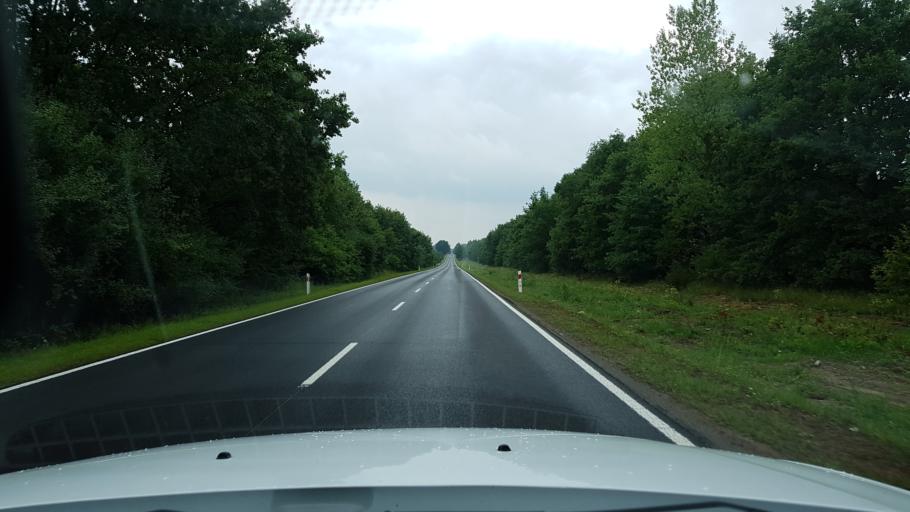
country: PL
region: West Pomeranian Voivodeship
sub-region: Powiat goleniowski
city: Maszewo
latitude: 53.4313
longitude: 15.0429
